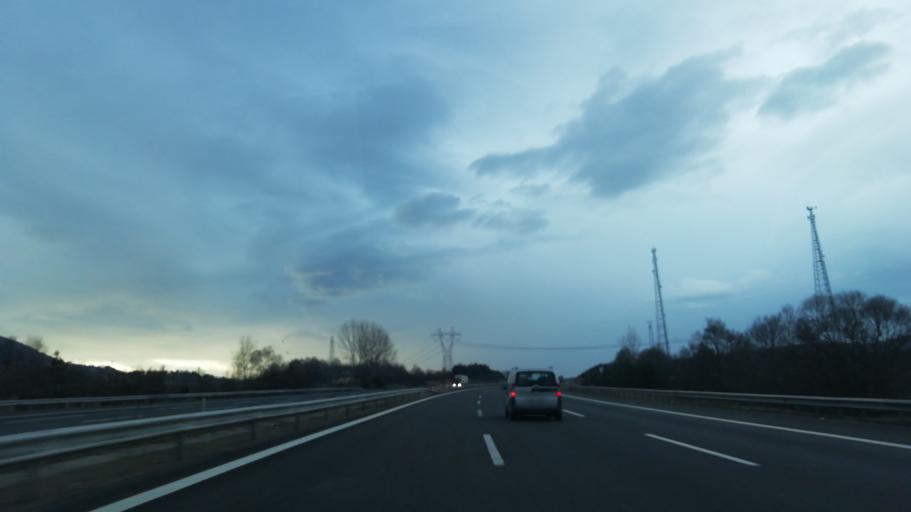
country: TR
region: Bolu
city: Yenicaga
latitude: 40.7509
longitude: 31.9327
